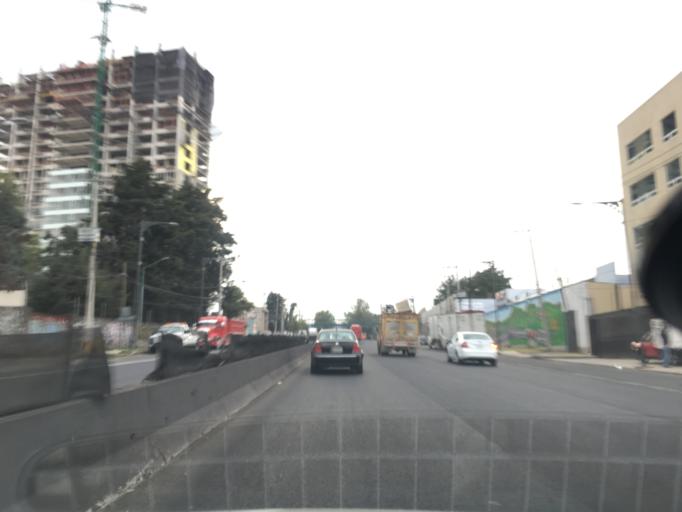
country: MX
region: Mexico City
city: Cuajimalpa
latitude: 19.3511
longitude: -99.2973
